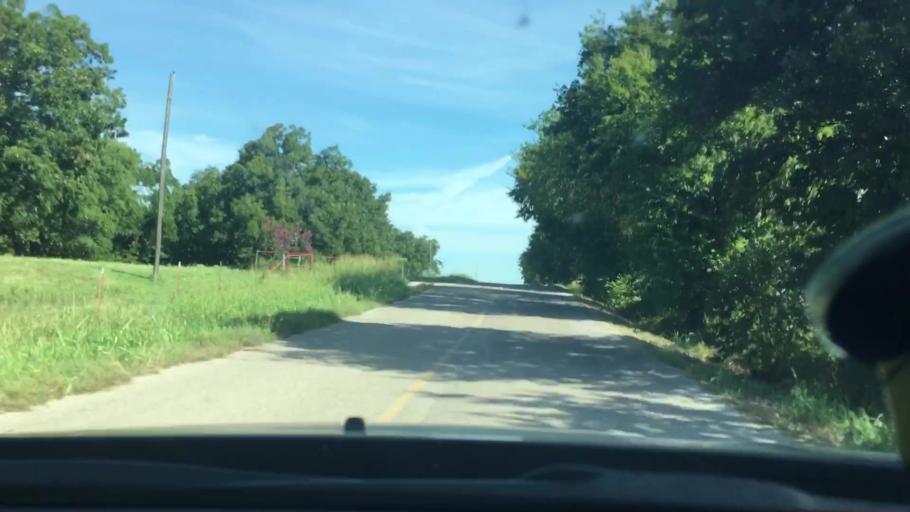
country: US
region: Oklahoma
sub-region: Carter County
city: Lone Grove
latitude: 34.2938
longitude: -97.2824
